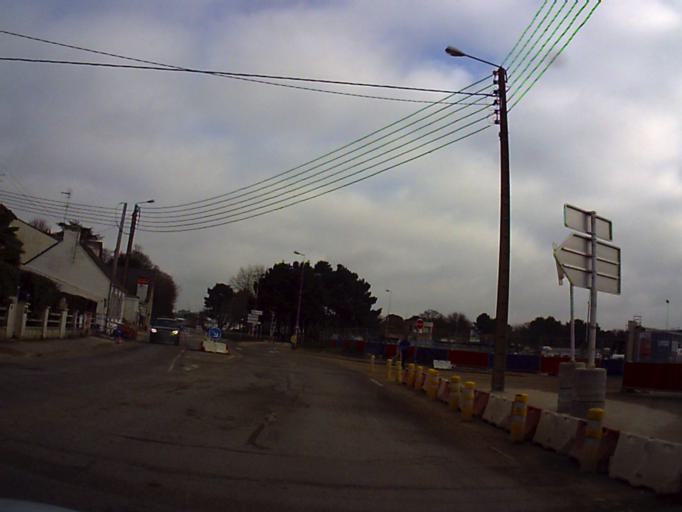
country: FR
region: Brittany
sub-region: Departement du Morbihan
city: Vannes
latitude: 47.6402
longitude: -2.7626
